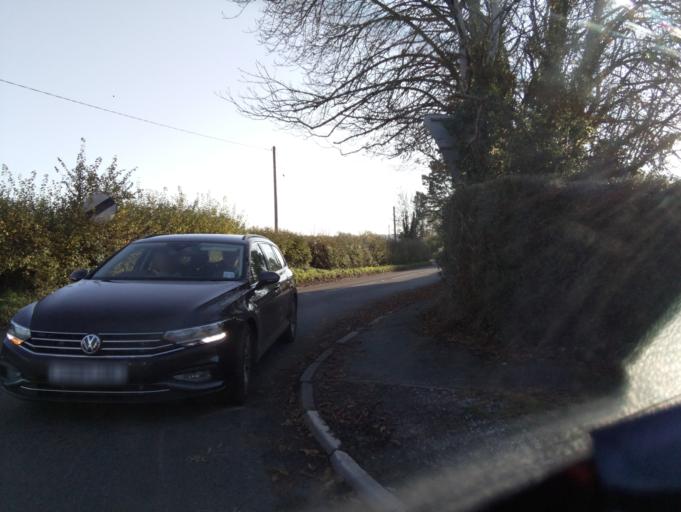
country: GB
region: England
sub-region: Dorset
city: Sherborne
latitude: 50.9565
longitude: -2.4997
